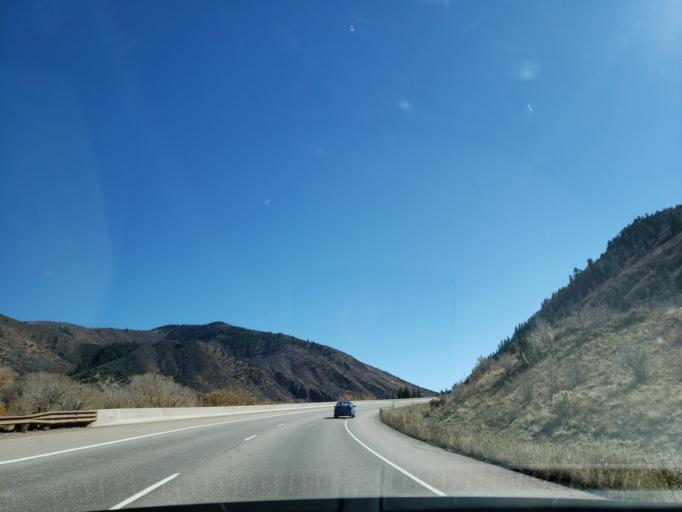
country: US
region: Colorado
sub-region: Eagle County
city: Basalt
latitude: 39.3233
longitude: -106.9478
